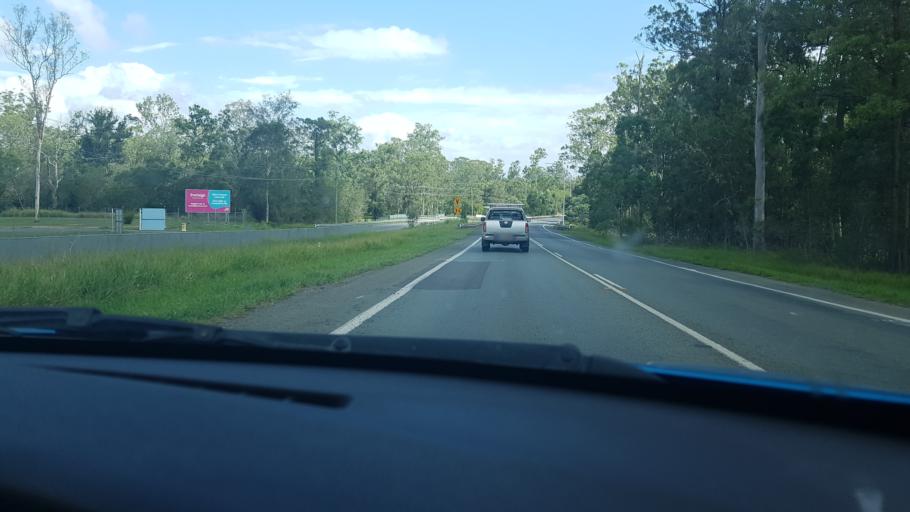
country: AU
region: Queensland
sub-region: Logan
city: North Maclean
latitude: -27.7496
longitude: 153.0258
